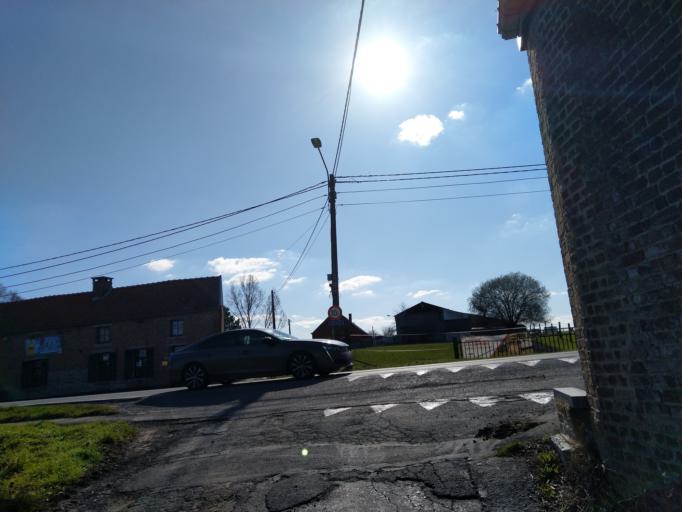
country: BE
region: Wallonia
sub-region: Province du Hainaut
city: Soignies
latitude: 50.5952
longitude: 4.0411
